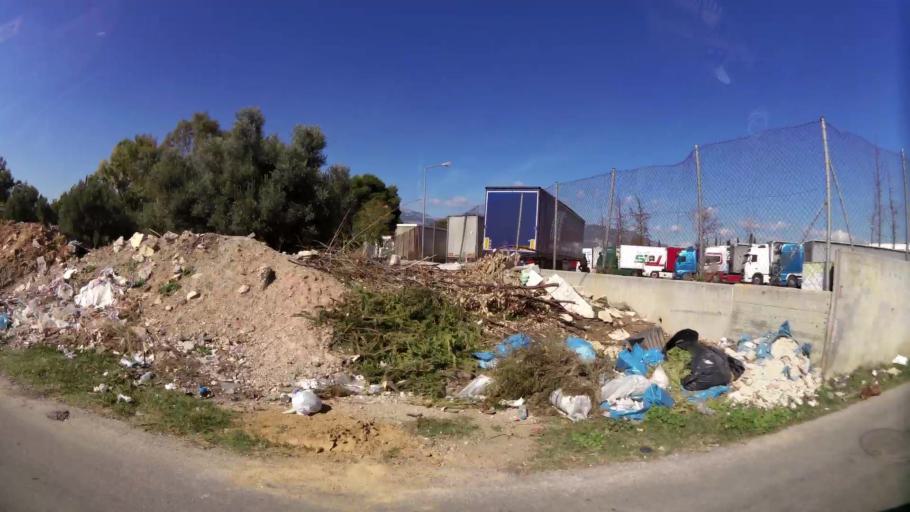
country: GR
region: Attica
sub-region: Nomarchia Athinas
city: Lykovrysi
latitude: 38.0847
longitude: 23.7814
